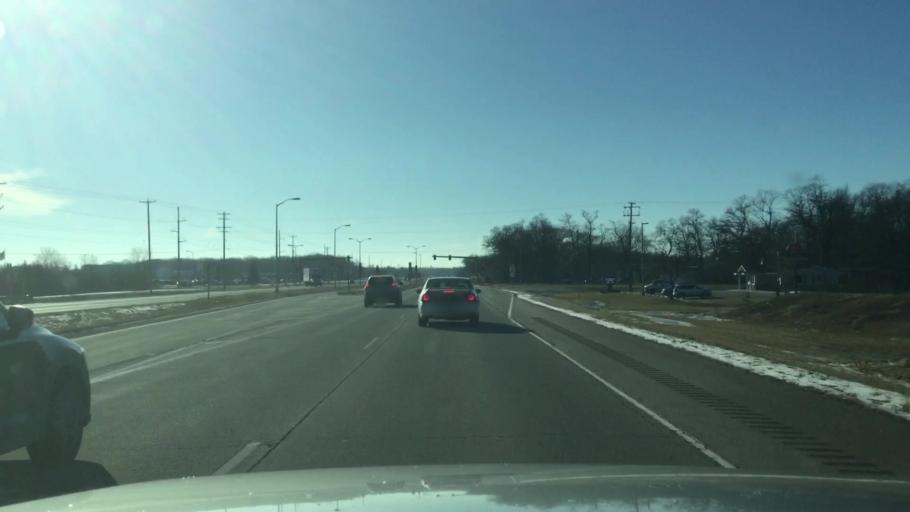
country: US
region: Wisconsin
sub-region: Racine County
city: Browns Lake
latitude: 42.7114
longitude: -88.2359
